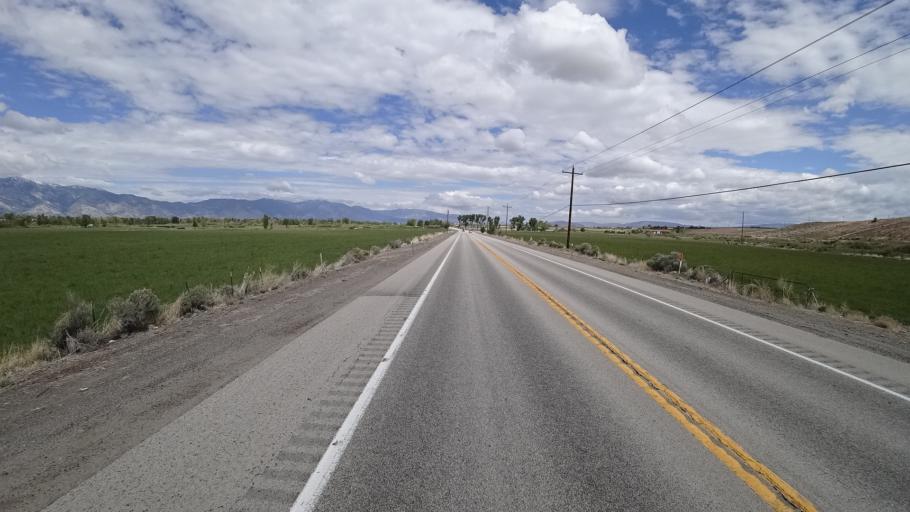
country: US
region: Nevada
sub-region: Douglas County
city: Gardnerville Ranchos
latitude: 38.8943
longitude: -119.7007
